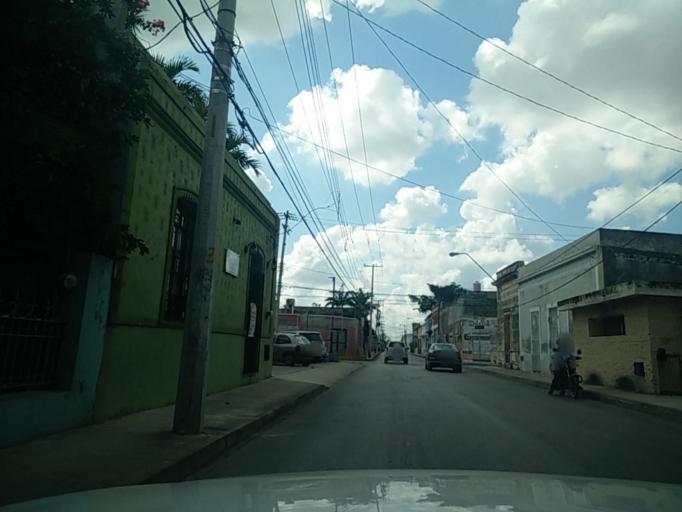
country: MX
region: Yucatan
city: Merida
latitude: 20.9786
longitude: -89.6224
